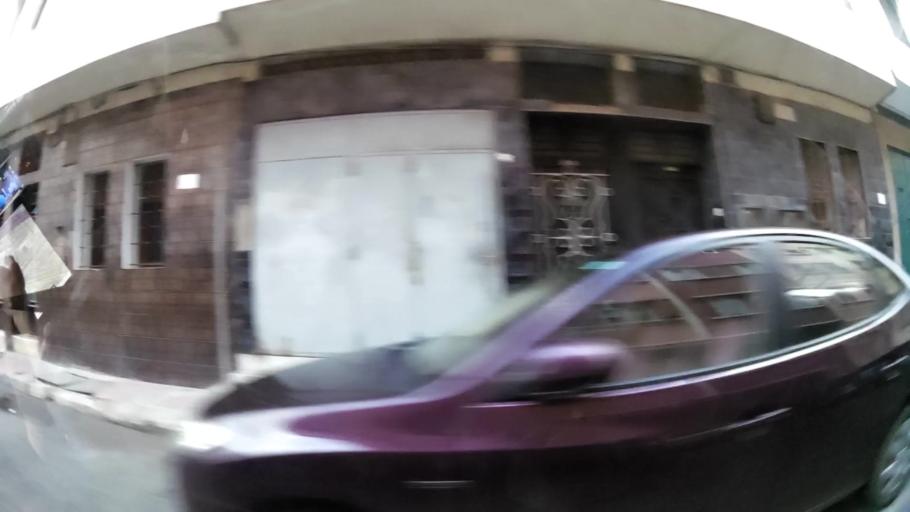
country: MA
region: Grand Casablanca
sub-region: Casablanca
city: Casablanca
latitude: 33.5583
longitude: -7.5976
